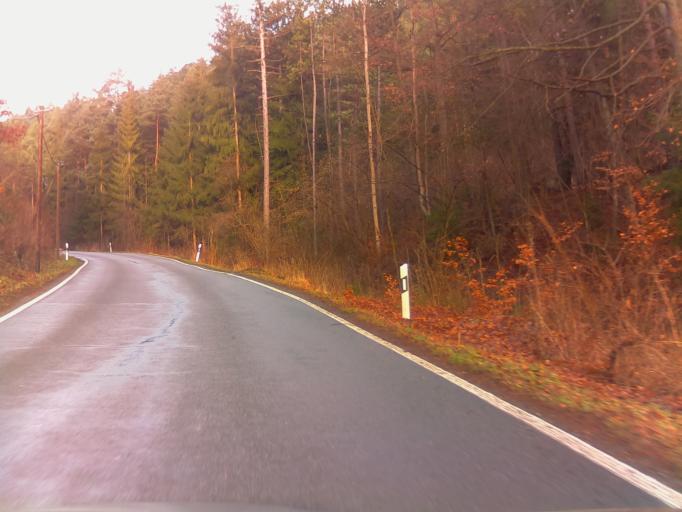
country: DE
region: Thuringia
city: Plaue
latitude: 50.8060
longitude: 10.9235
